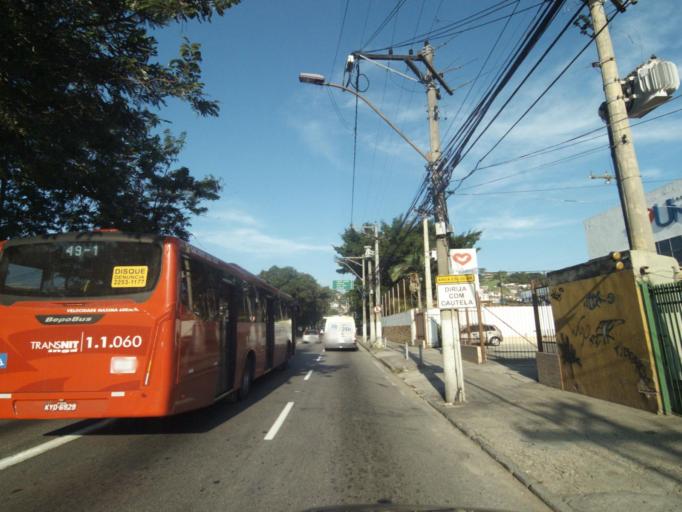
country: BR
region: Rio de Janeiro
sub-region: Niteroi
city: Niteroi
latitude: -22.8816
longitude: -43.0826
